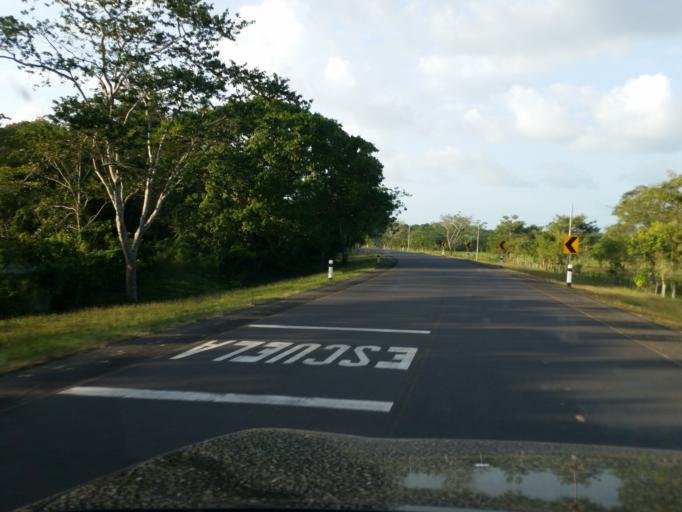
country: NI
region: Rio San Juan
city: San Carlos
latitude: 11.3070
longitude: -84.7273
